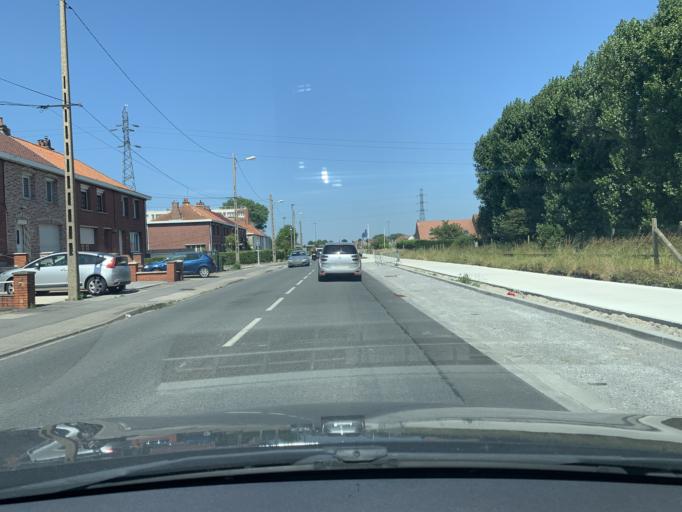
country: FR
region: Nord-Pas-de-Calais
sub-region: Departement du Nord
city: Coudekerque-Branche
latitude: 51.0253
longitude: 2.3999
